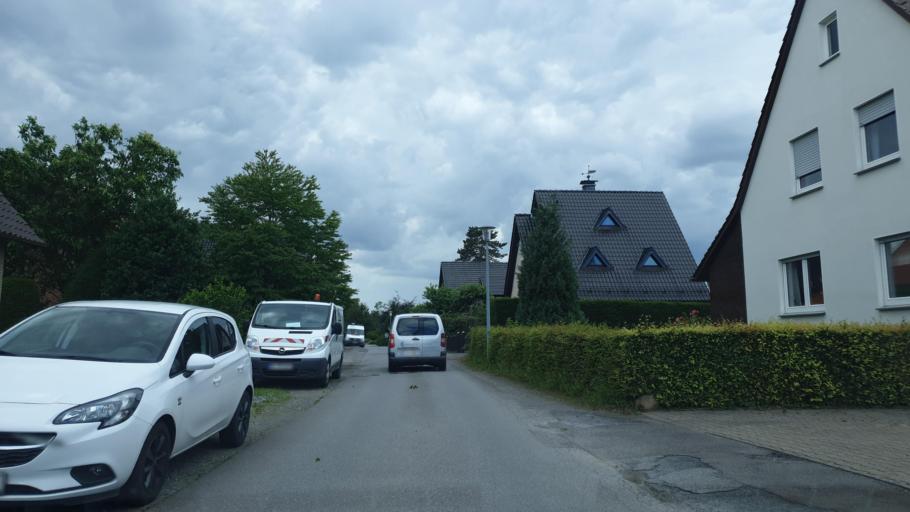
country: DE
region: North Rhine-Westphalia
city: Bad Oeynhausen
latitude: 52.1837
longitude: 8.8032
